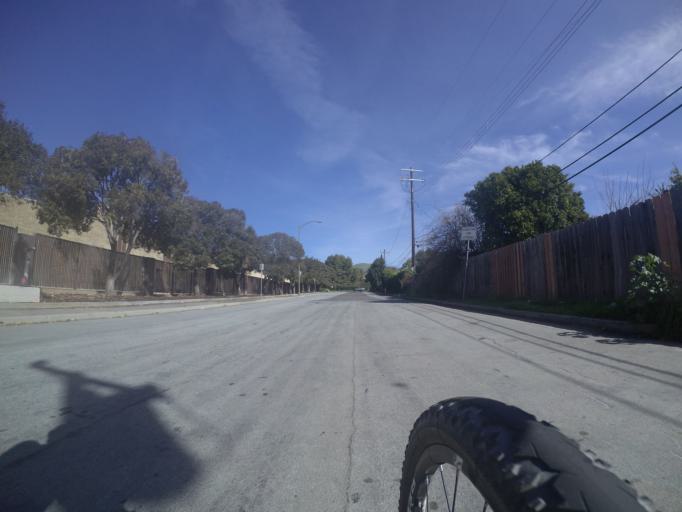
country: US
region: California
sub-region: Santa Clara County
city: Milpitas
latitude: 37.4132
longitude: -121.8752
